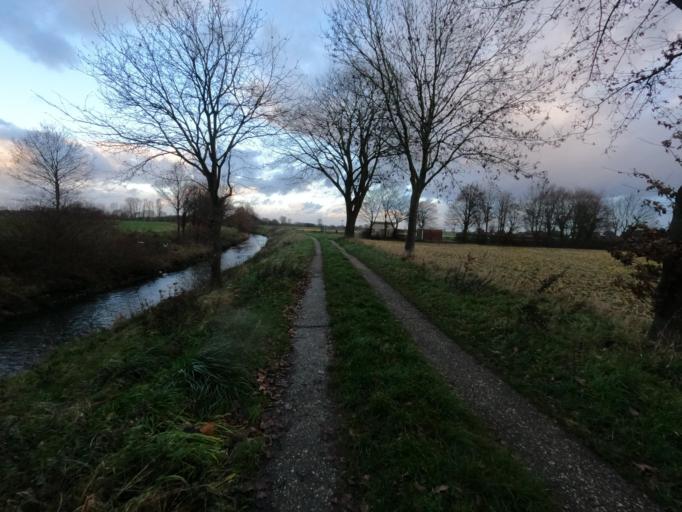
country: DE
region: North Rhine-Westphalia
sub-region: Regierungsbezirk Koln
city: Heinsberg
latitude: 51.0717
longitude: 6.1134
